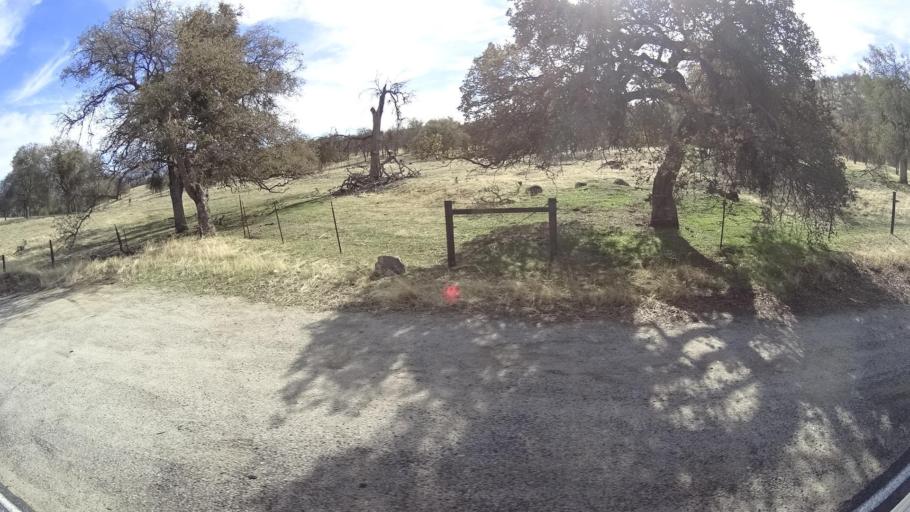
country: US
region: California
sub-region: Kern County
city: Alta Sierra
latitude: 35.6462
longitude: -118.7829
